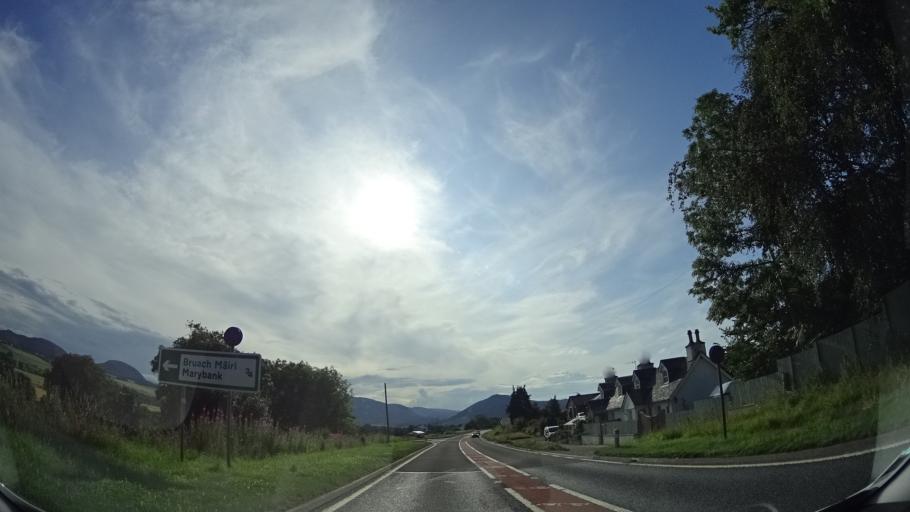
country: GB
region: Scotland
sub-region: Highland
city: Muir of Ord
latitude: 57.5580
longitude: -4.5371
